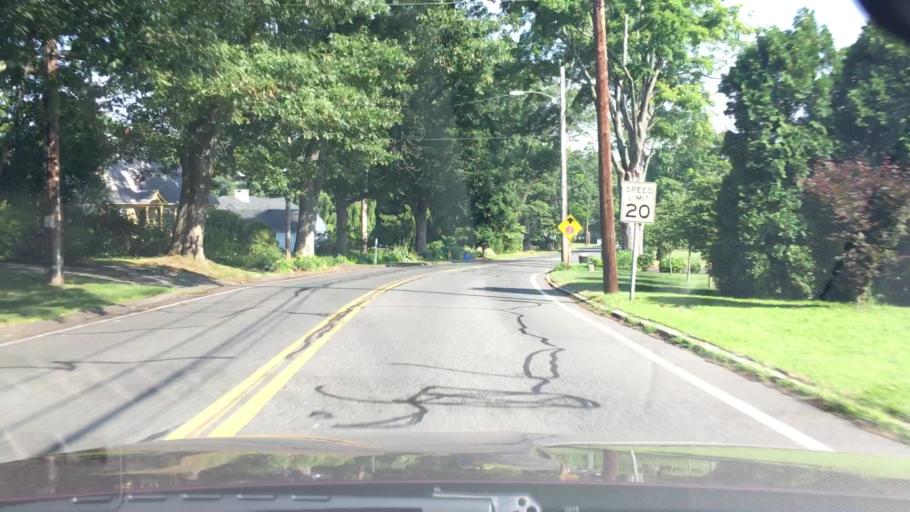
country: US
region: Massachusetts
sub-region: Hampden County
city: East Longmeadow
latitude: 42.0527
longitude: -72.5106
